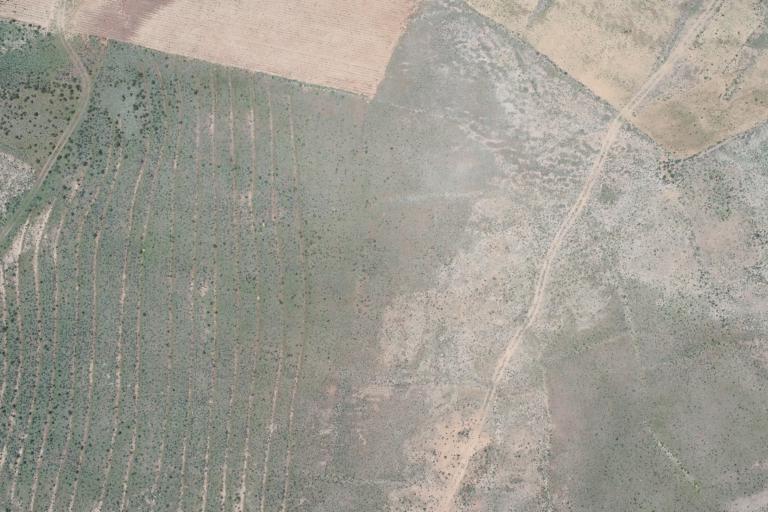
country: BO
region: La Paz
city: Curahuara de Carangas
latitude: -17.3106
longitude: -68.5200
